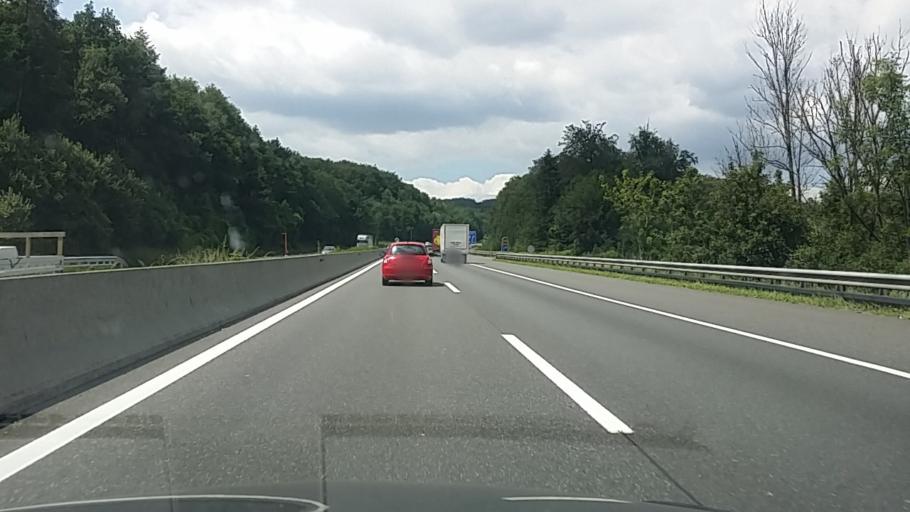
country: AT
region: Lower Austria
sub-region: Politischer Bezirk Baden
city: Klausen-Leopoldsdorf
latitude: 48.1123
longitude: 15.9754
